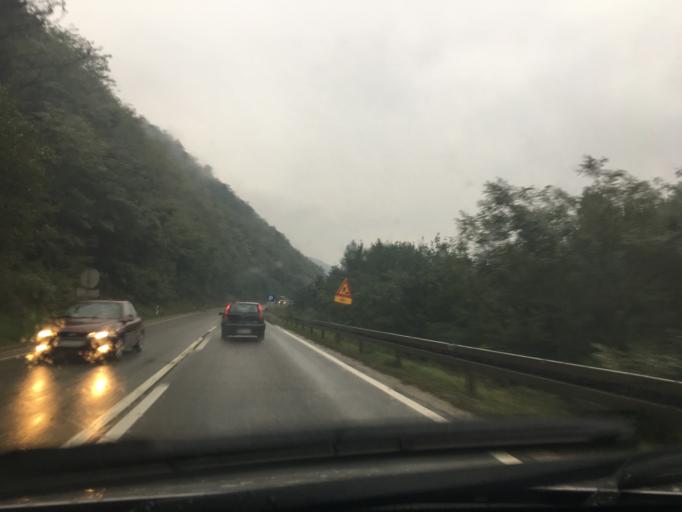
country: RS
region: Central Serbia
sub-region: Pcinjski Okrug
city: Vladicin Han
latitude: 42.7614
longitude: 22.0843
